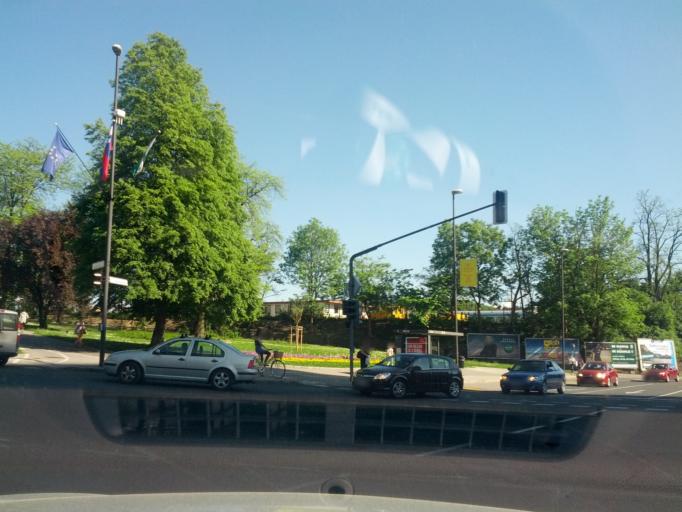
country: SI
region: Ljubljana
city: Ljubljana
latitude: 46.0598
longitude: 14.5209
